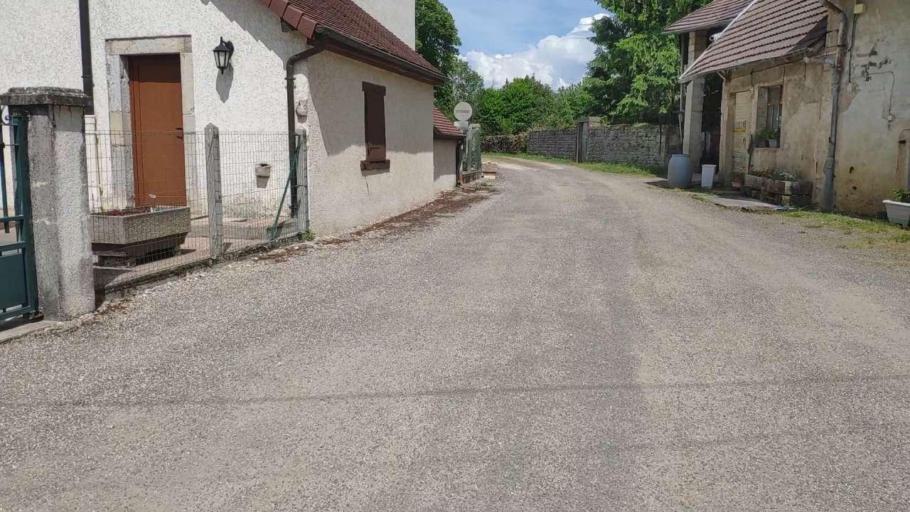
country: FR
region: Franche-Comte
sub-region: Departement du Jura
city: Bletterans
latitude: 46.7459
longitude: 5.4934
